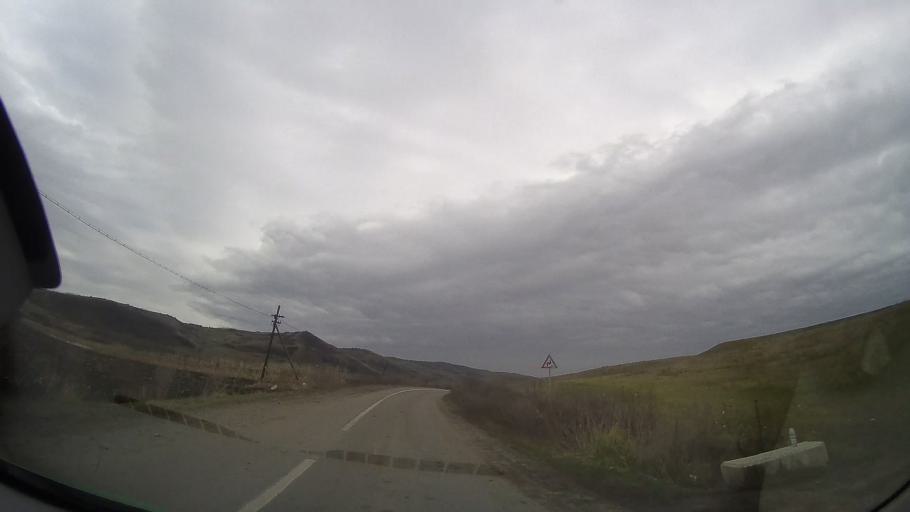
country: RO
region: Mures
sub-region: Comuna Craesti
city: Craiesti
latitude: 46.7853
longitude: 24.4248
